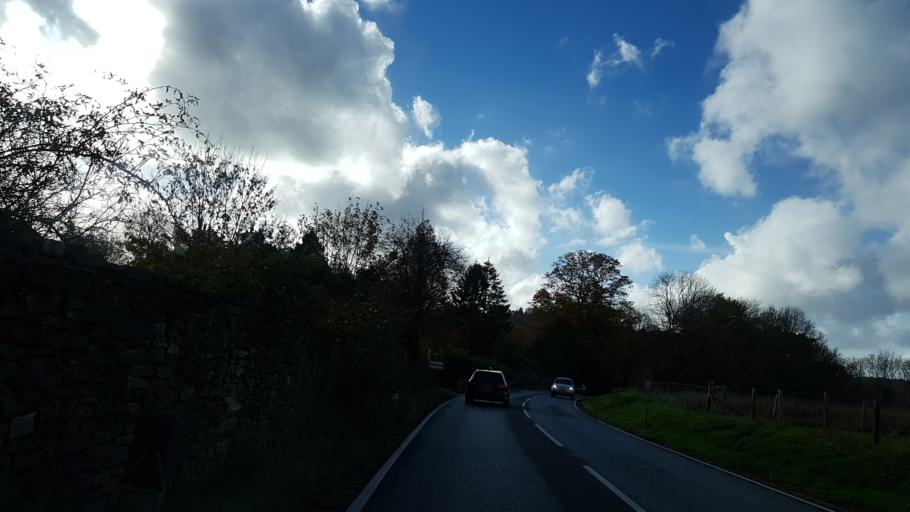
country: GB
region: England
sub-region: Surrey
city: Haslemere
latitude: 51.1088
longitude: -0.6869
